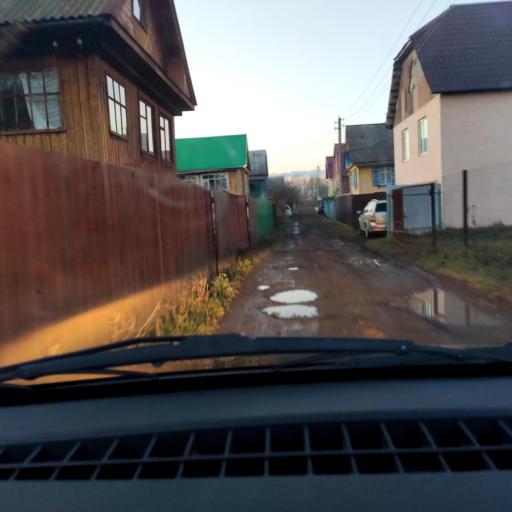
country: RU
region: Bashkortostan
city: Ufa
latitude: 54.6481
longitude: 55.8992
